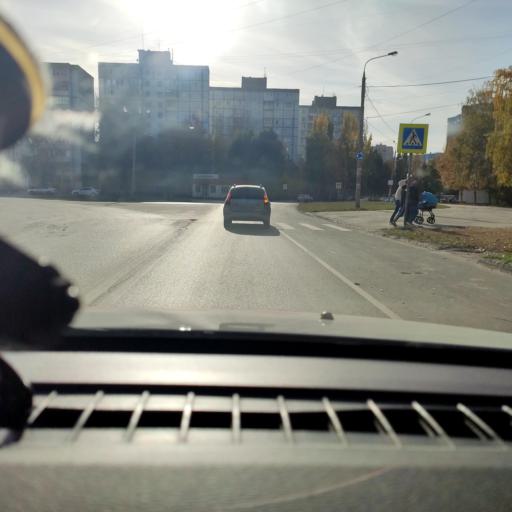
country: RU
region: Samara
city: Samara
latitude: 53.2615
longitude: 50.2298
